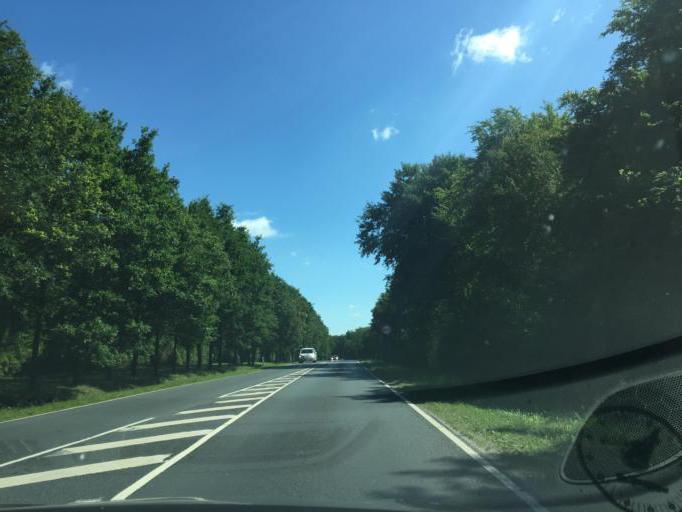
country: DK
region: South Denmark
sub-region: Odense Kommune
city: Bellinge
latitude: 55.3750
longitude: 10.3351
